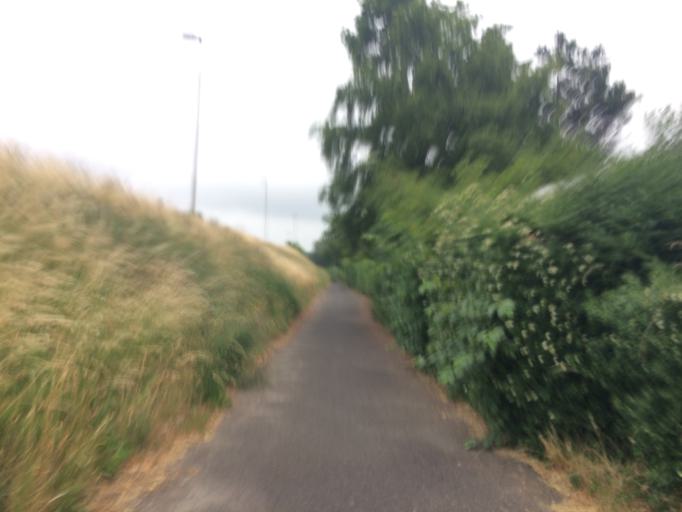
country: DK
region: Capital Region
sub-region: Bornholm Kommune
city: Ronne
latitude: 55.0997
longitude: 14.7171
